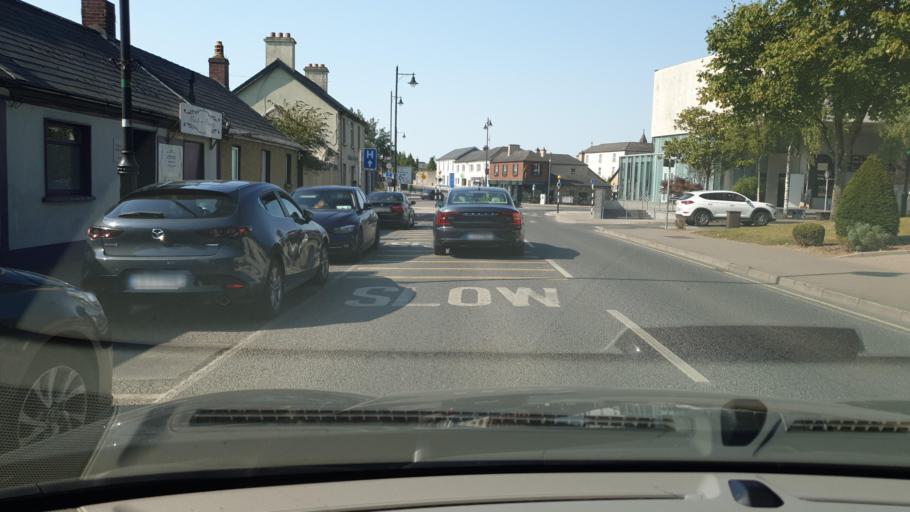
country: IE
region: Leinster
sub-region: An Mhi
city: Navan
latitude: 53.6497
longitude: -6.6862
